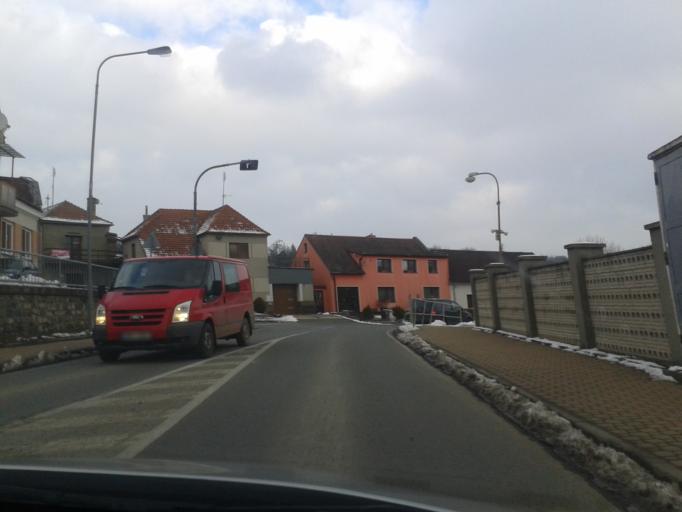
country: CZ
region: Olomoucky
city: Konice
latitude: 49.5916
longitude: 16.8885
